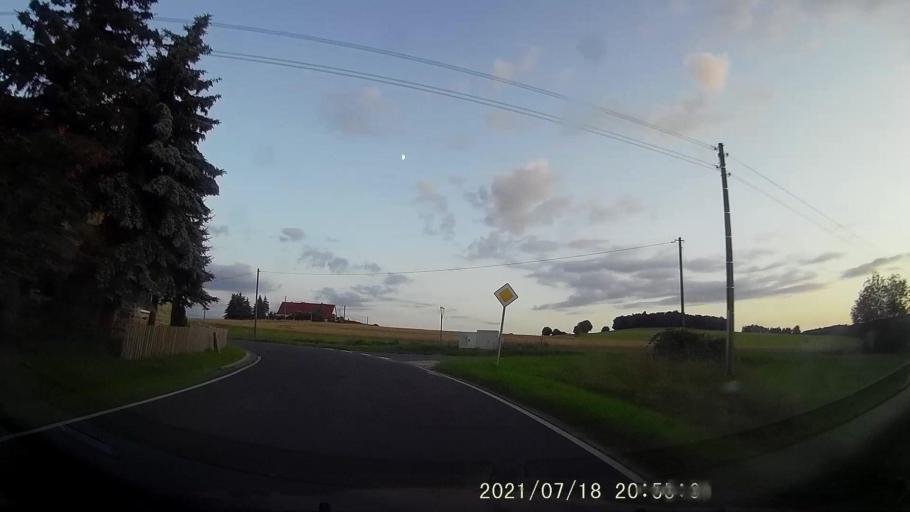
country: DE
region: Saxony
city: Konigshain
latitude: 51.1807
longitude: 14.8774
